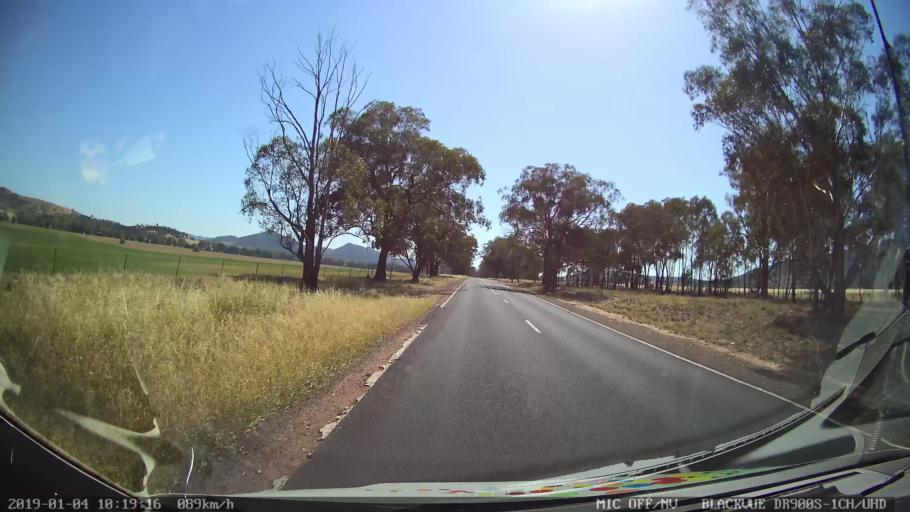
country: AU
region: New South Wales
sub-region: Cabonne
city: Canowindra
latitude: -33.3775
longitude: 148.4783
